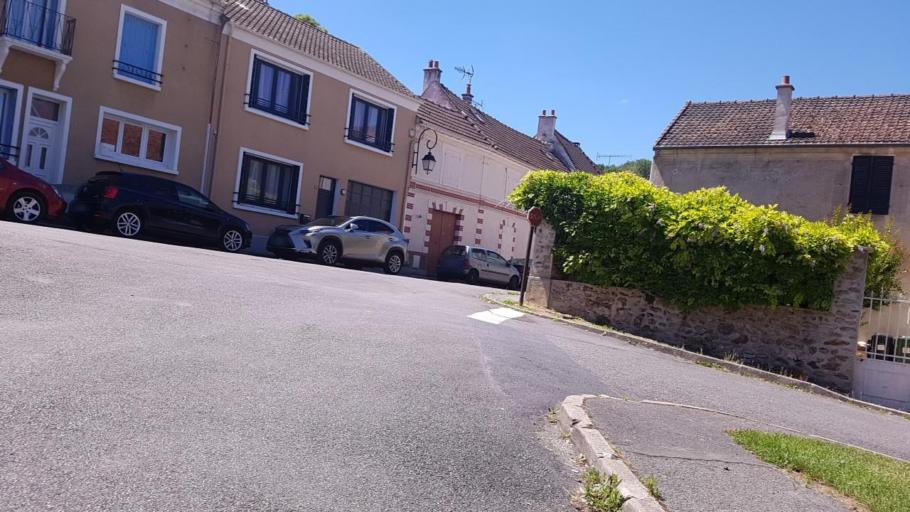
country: FR
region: Ile-de-France
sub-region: Departement de Seine-et-Marne
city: Saint-Jean-les-Deux-Jumeaux
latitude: 48.9506
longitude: 3.0188
